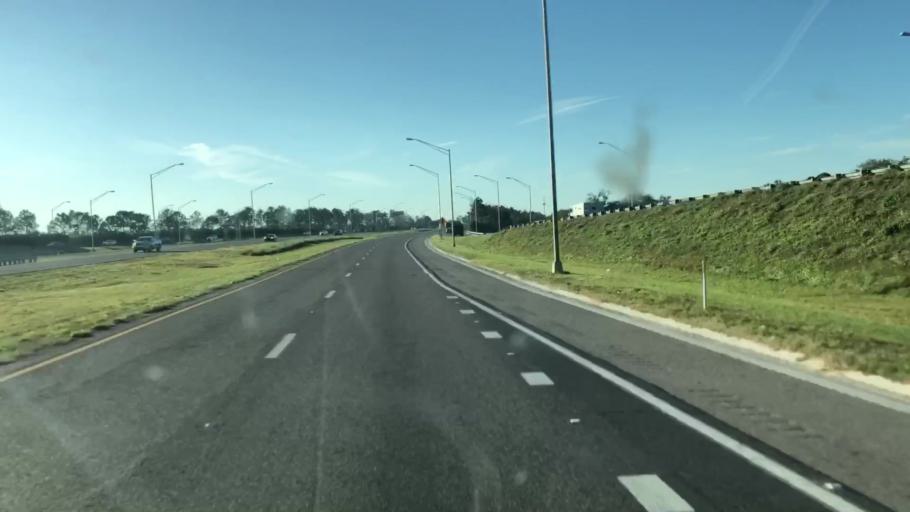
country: US
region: Florida
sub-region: Orange County
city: Ocoee
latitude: 28.5434
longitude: -81.5574
